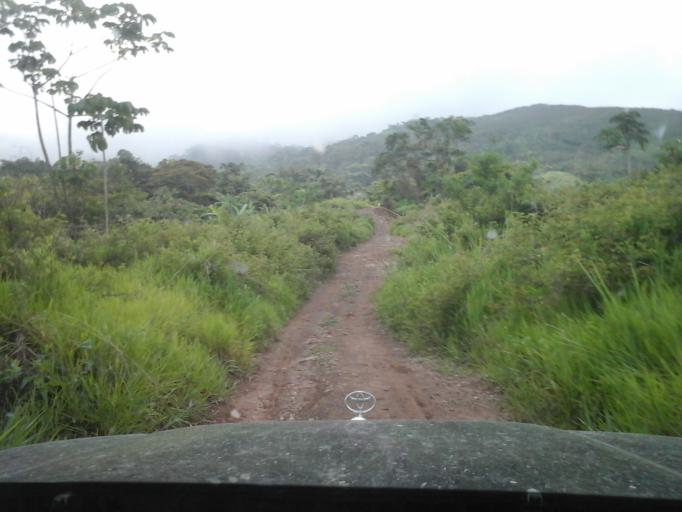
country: CO
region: Cesar
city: Agustin Codazzi
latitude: 9.9541
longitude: -73.0658
